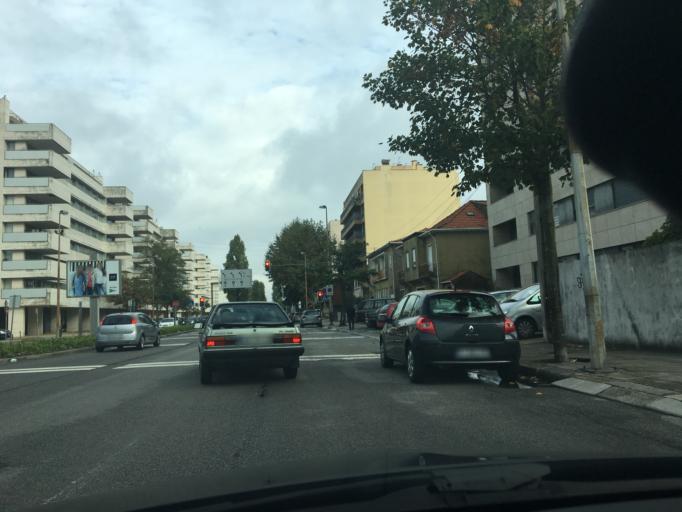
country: PT
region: Porto
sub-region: Matosinhos
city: Senhora da Hora
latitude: 41.1806
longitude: -8.6527
